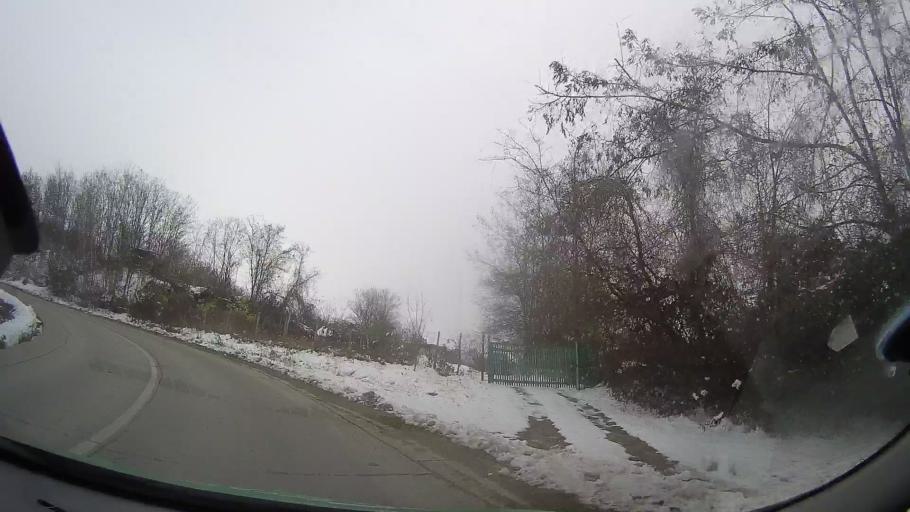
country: RO
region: Bacau
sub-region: Comuna Podu Turcului
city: Podu Turcului
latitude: 46.2016
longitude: 27.3925
